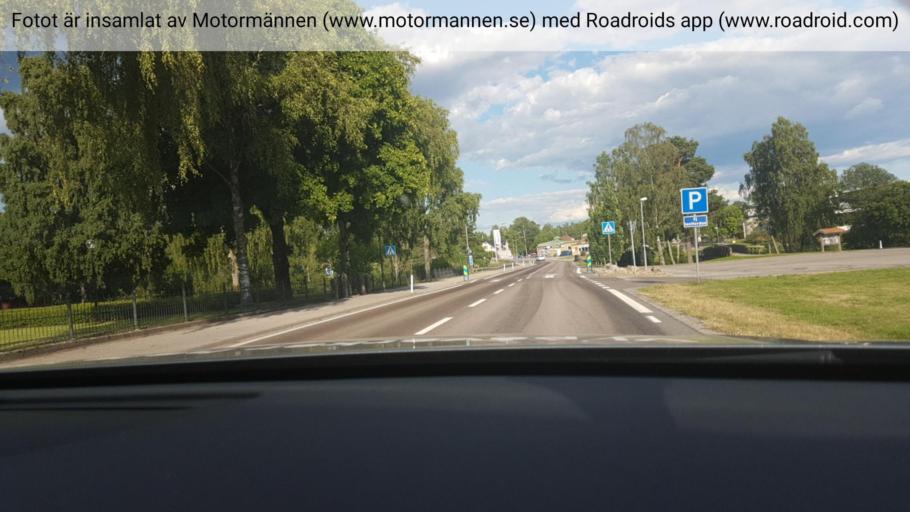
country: SE
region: Vaestra Goetaland
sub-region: Tranemo Kommun
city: Tranemo
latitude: 57.4869
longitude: 13.3462
